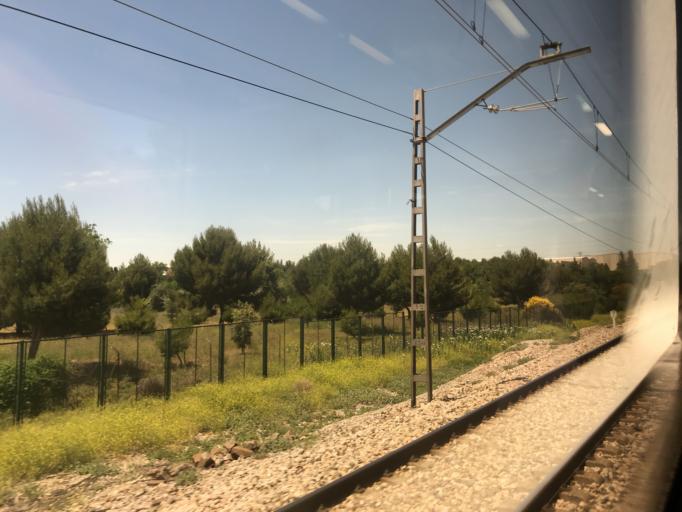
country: ES
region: Madrid
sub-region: Provincia de Madrid
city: Pinto
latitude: 40.2654
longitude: -3.7046
